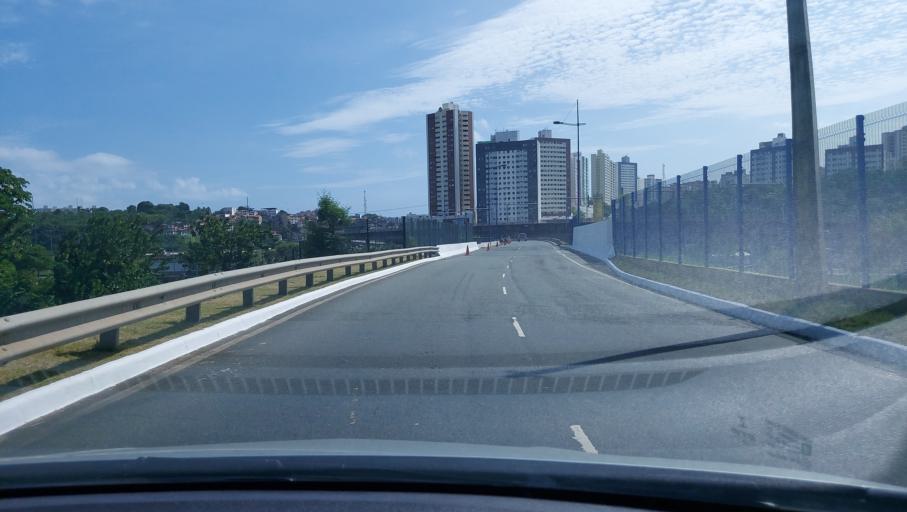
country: BR
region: Bahia
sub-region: Salvador
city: Salvador
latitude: -12.9708
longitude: -38.4765
